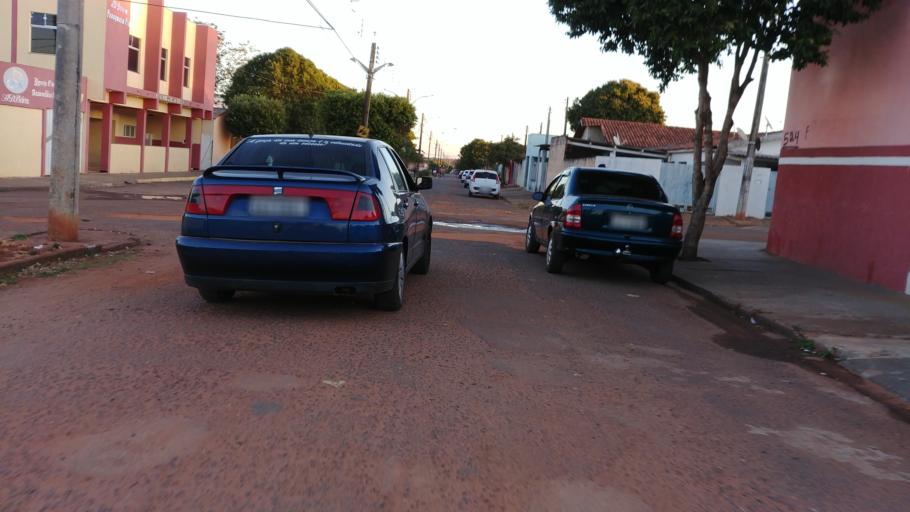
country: BR
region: Sao Paulo
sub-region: Paraguacu Paulista
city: Paraguacu Paulista
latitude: -22.4287
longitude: -50.5743
